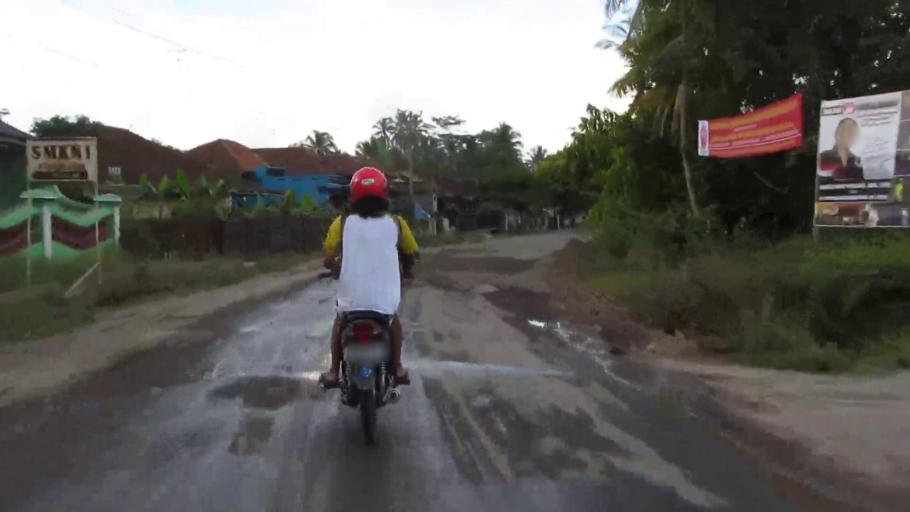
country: ID
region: West Java
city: Binangun
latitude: -7.7177
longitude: 108.4753
